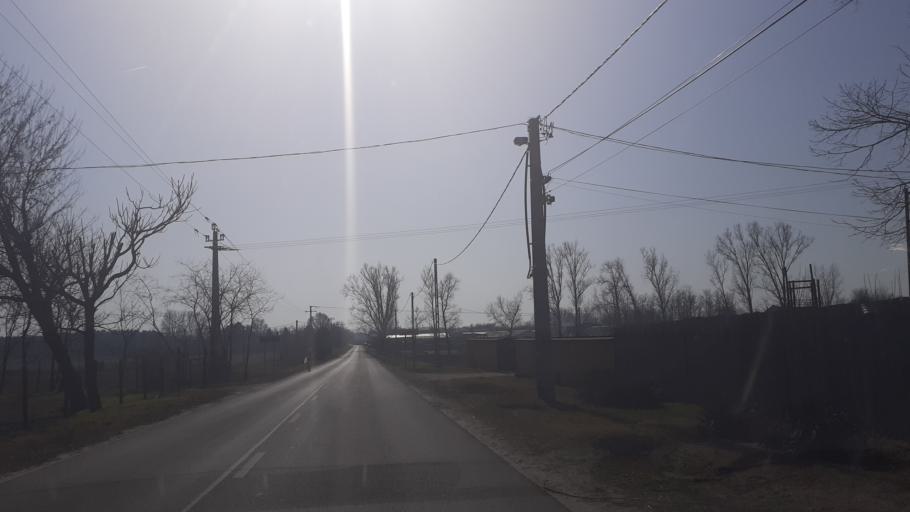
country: HU
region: Pest
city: Dabas
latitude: 47.1619
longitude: 19.3329
